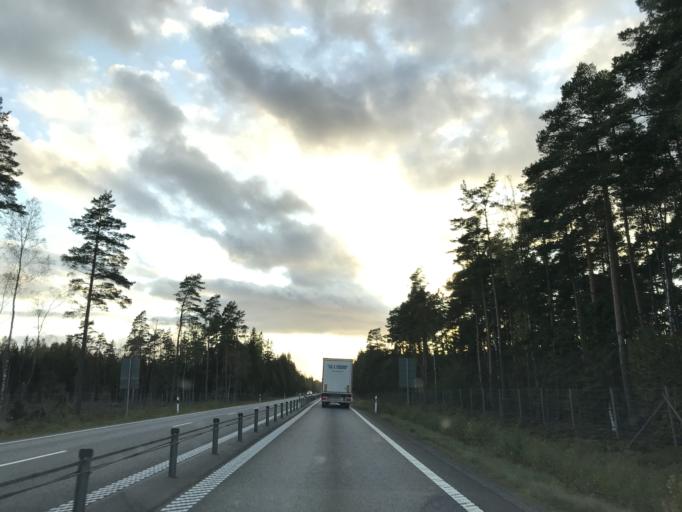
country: SE
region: Kronoberg
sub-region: Alvesta Kommun
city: Vislanda
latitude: 56.7116
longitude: 14.4336
